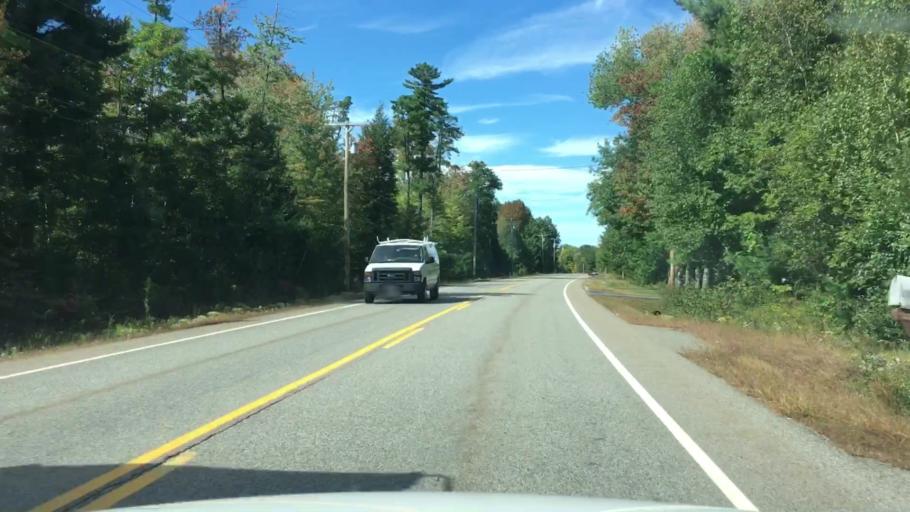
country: US
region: Maine
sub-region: Cumberland County
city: Westbrook
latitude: 43.6525
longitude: -70.3985
